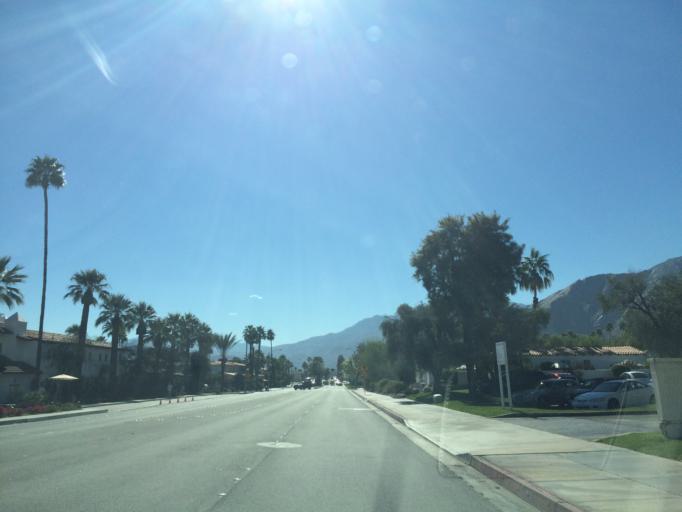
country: US
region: California
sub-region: Riverside County
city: Palm Springs
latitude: 33.8332
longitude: -116.5457
